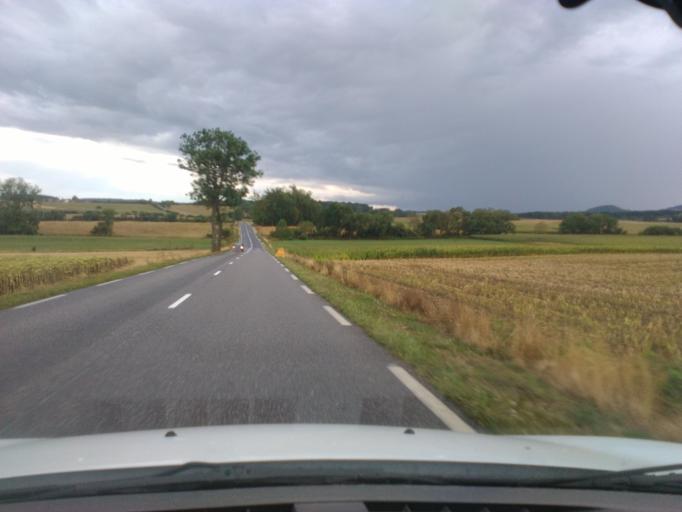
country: FR
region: Lorraine
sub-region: Departement de Meurthe-et-Moselle
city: Vezelise
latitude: 48.4375
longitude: 6.1255
